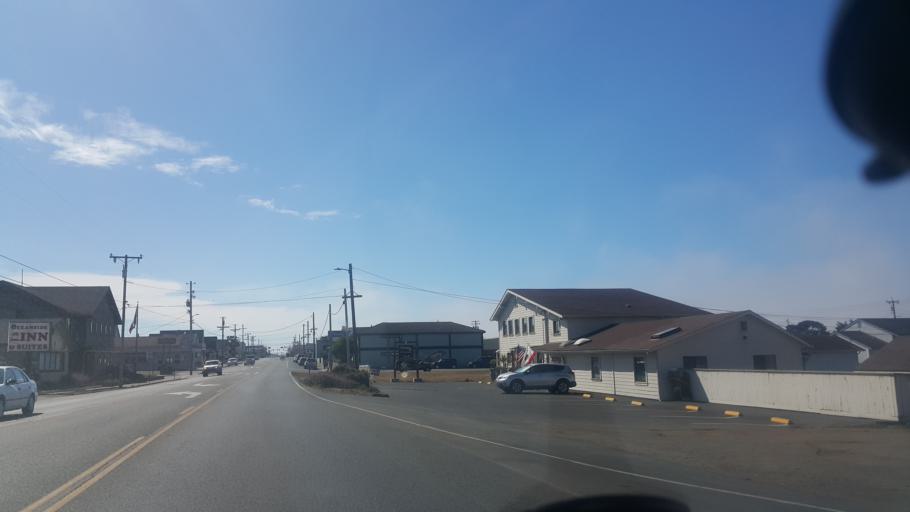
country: US
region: California
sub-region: Mendocino County
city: Fort Bragg
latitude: 39.4515
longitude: -123.8060
